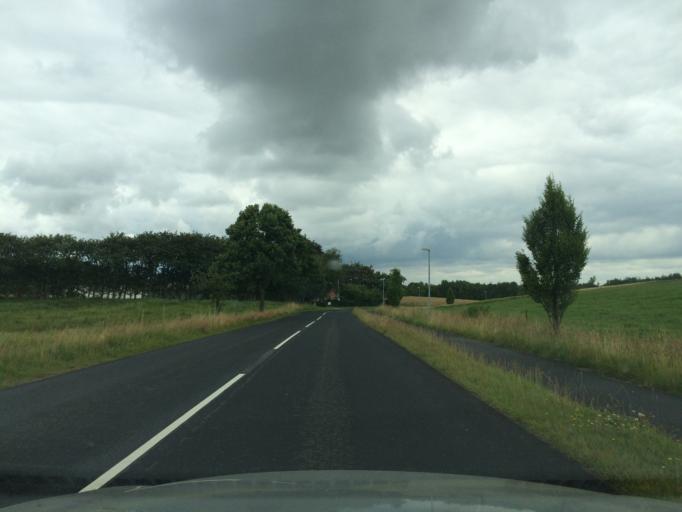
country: DK
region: Central Jutland
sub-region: Favrskov Kommune
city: Hammel
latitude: 56.2165
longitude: 9.7428
